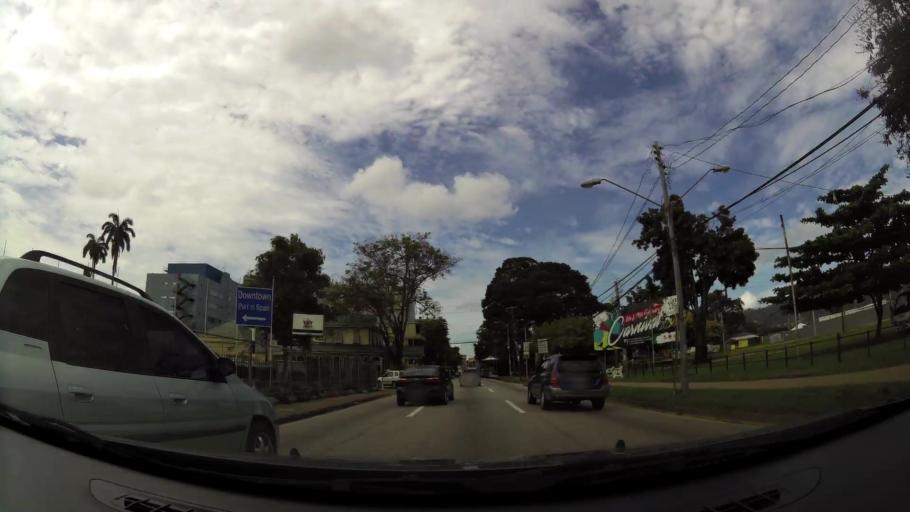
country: TT
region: City of Port of Spain
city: Port-of-Spain
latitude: 10.6641
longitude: -61.5129
